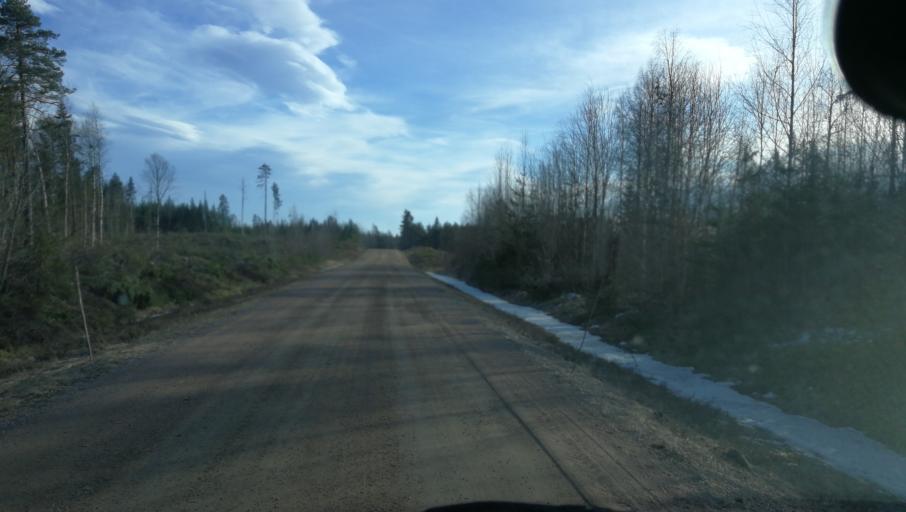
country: SE
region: Dalarna
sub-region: Vansbro Kommun
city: Vansbro
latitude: 60.8264
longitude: 14.1942
